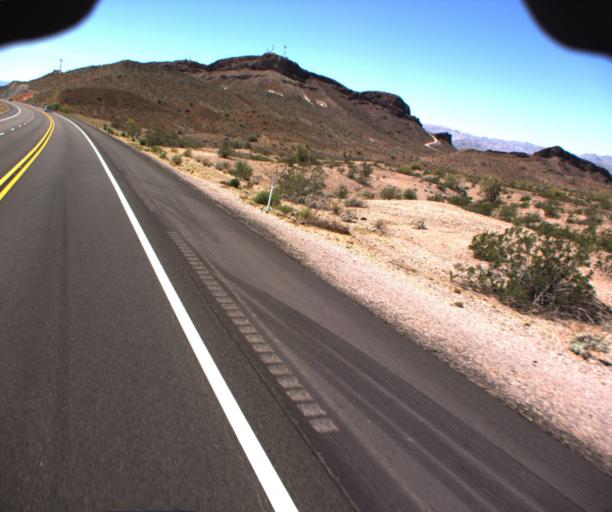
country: US
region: Arizona
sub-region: Mohave County
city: Desert Hills
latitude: 34.6062
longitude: -114.3611
